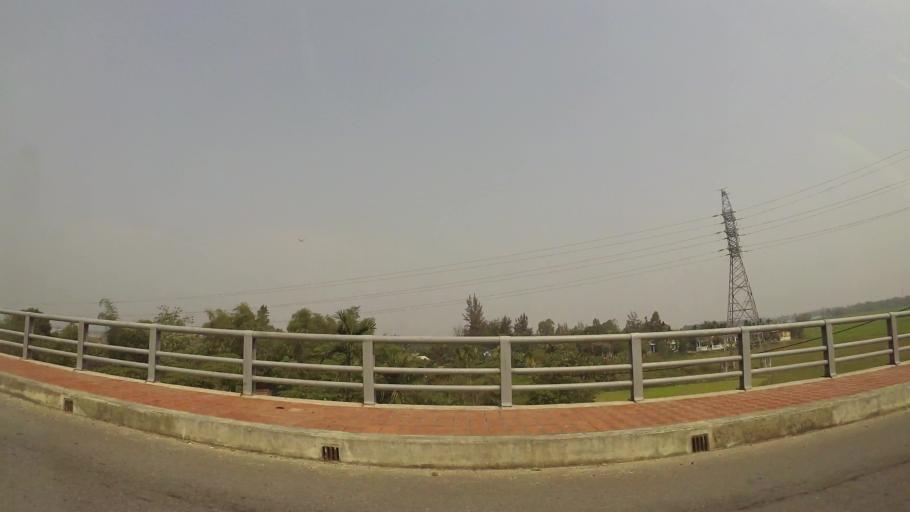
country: VN
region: Da Nang
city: Cam Le
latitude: 15.9696
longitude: 108.2186
